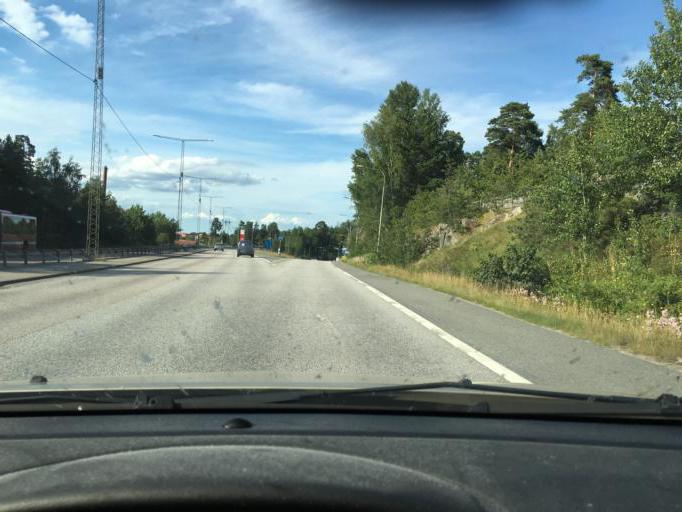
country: SE
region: Stockholm
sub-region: Nacka Kommun
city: Boo
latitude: 59.3206
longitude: 18.2573
